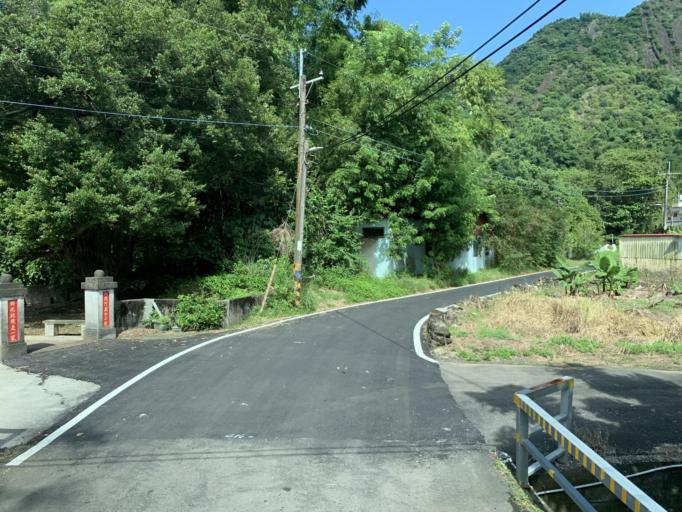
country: TW
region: Taiwan
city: Yujing
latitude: 22.9016
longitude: 120.5170
